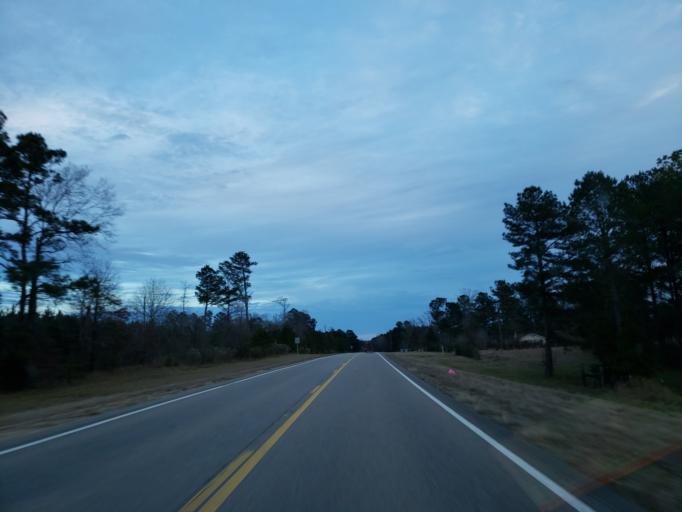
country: US
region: Mississippi
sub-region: Kemper County
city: De Kalb
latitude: 32.8310
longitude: -88.3648
